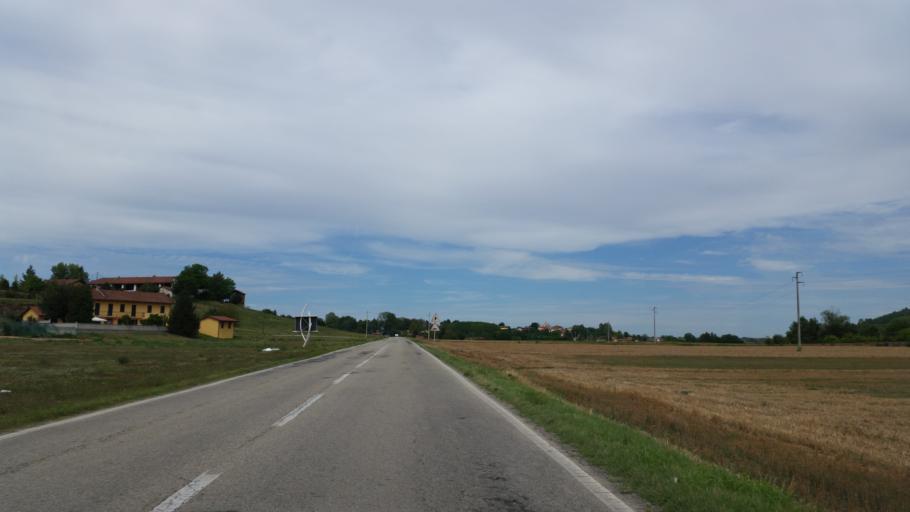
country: IT
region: Piedmont
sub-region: Provincia di Asti
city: Celle Enomondo
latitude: 44.8836
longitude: 8.1346
